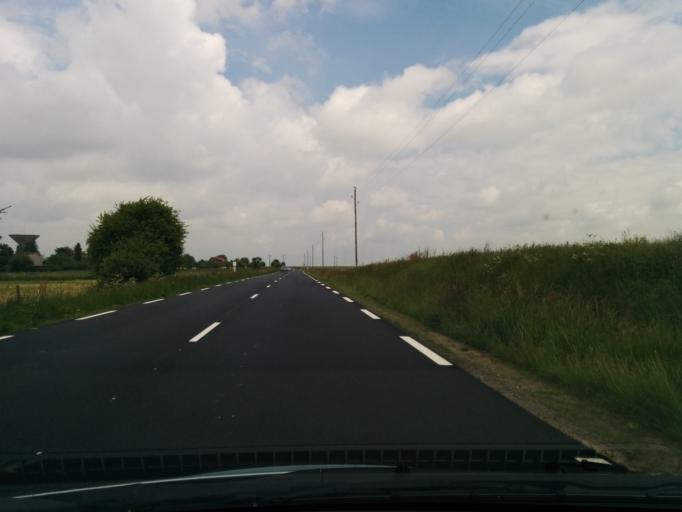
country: FR
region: Ile-de-France
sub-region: Departement des Yvelines
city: Limetz-Villez
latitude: 49.1402
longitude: 1.5314
